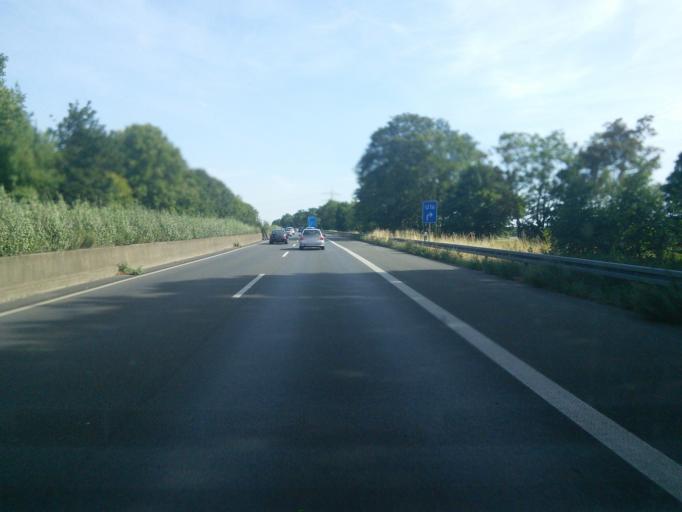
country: DE
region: North Rhine-Westphalia
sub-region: Regierungsbezirk Dusseldorf
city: Dormagen
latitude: 51.0925
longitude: 6.8057
